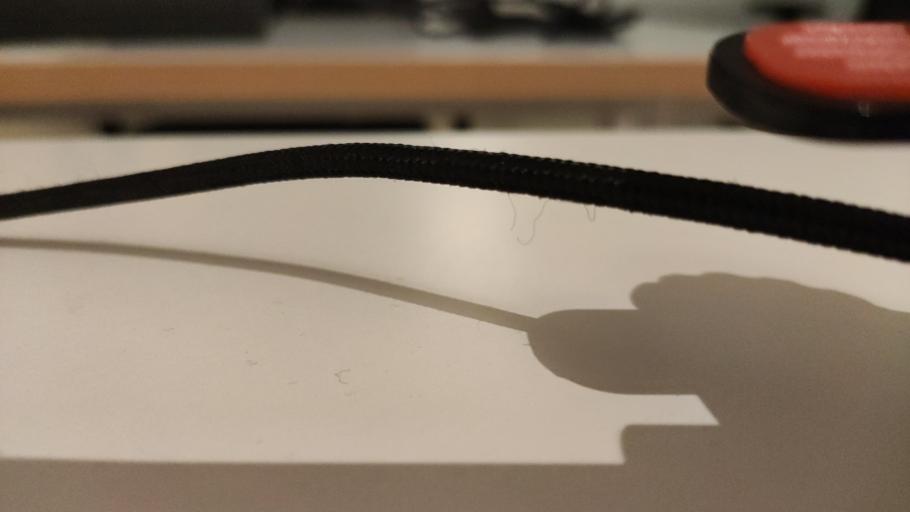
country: RU
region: Moskovskaya
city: Malino
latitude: 55.1077
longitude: 38.1044
